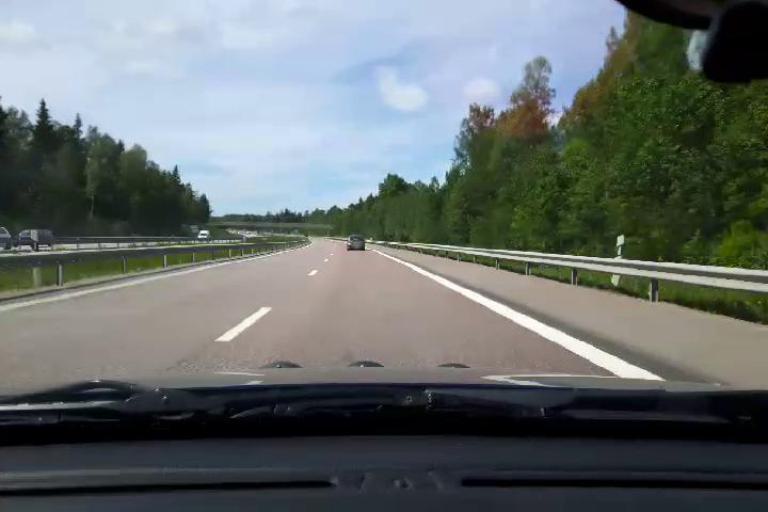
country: SE
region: Gaevleborg
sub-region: Gavle Kommun
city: Gavle
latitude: 60.6634
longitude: 17.1095
